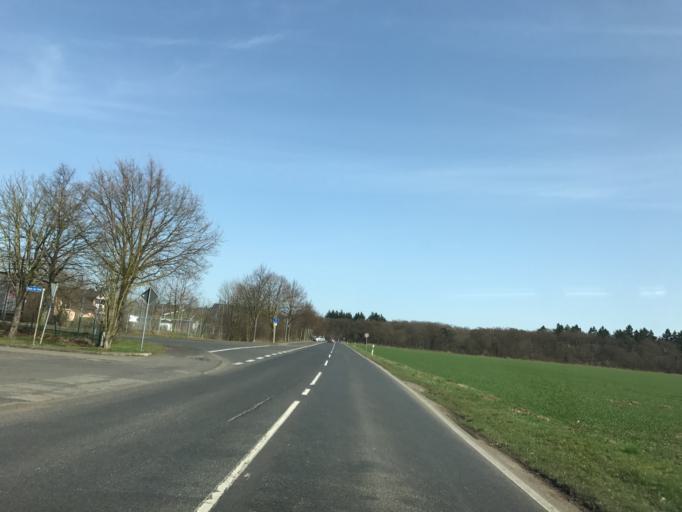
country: DE
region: North Rhine-Westphalia
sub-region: Regierungsbezirk Koln
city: Rheinbach
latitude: 50.6653
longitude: 6.9586
